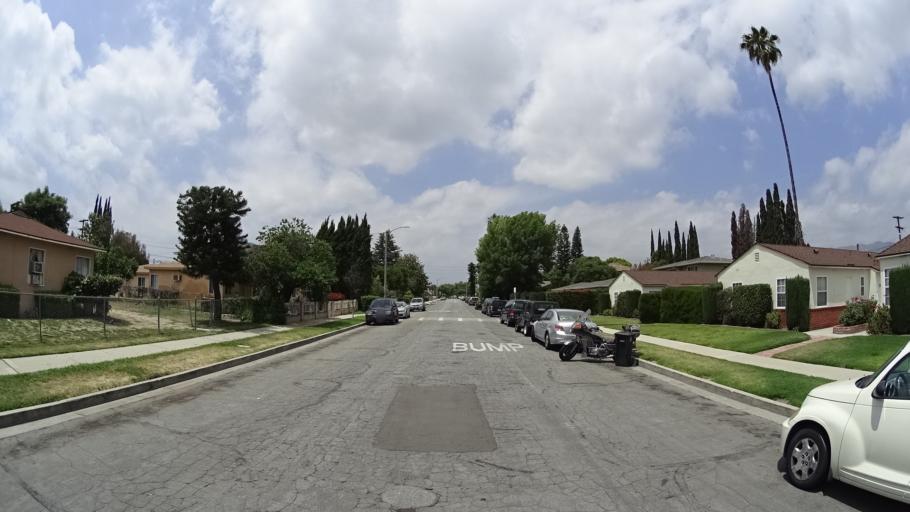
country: US
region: California
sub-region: Los Angeles County
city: Universal City
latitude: 34.1619
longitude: -118.3336
